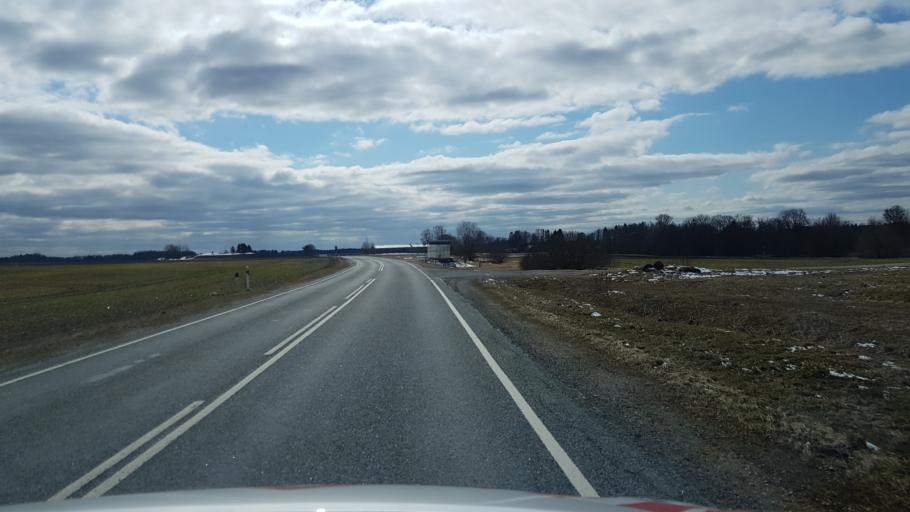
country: EE
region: Laeaene-Virumaa
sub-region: Tapa vald
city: Tapa
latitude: 59.3099
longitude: 26.0011
